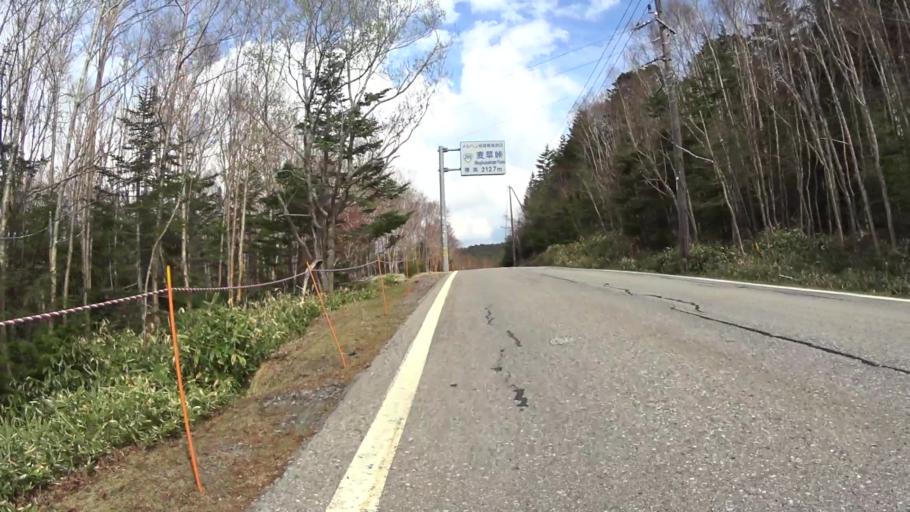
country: JP
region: Nagano
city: Saku
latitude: 36.0585
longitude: 138.3525
